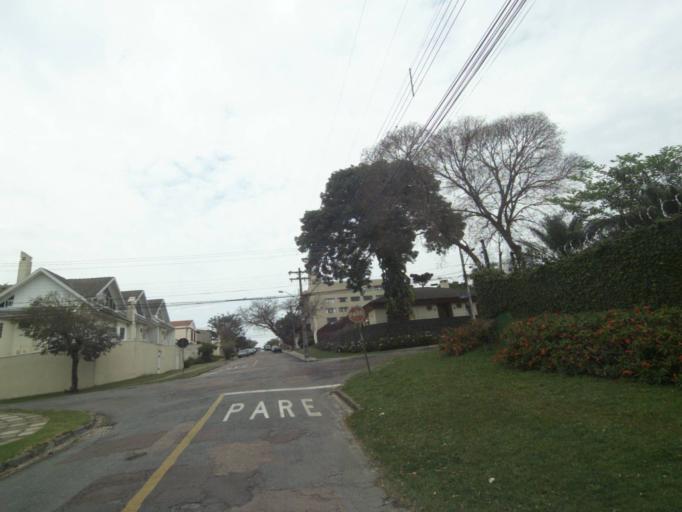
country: BR
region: Parana
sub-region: Curitiba
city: Curitiba
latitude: -25.4550
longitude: -49.3080
